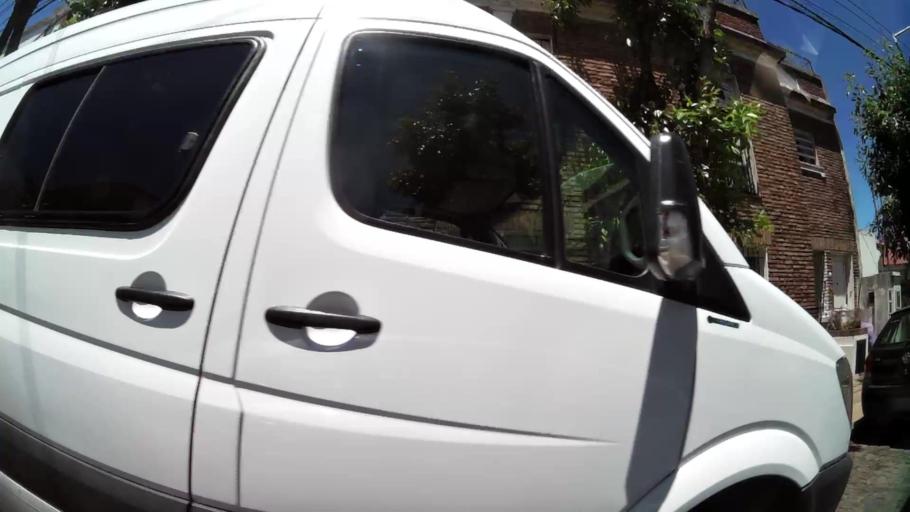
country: AR
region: Buenos Aires
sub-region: Partido de Tigre
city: Tigre
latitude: -34.4445
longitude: -58.5529
